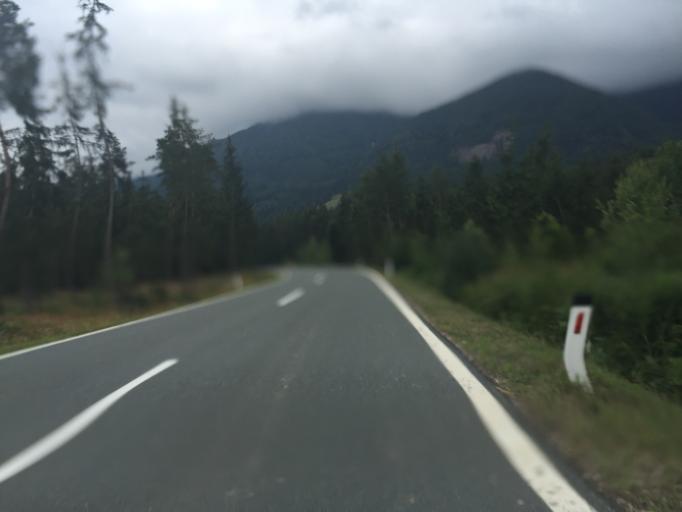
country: AT
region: Carinthia
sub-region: Politischer Bezirk Volkermarkt
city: Feistritz ob Bleiburg
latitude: 46.5511
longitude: 14.7699
